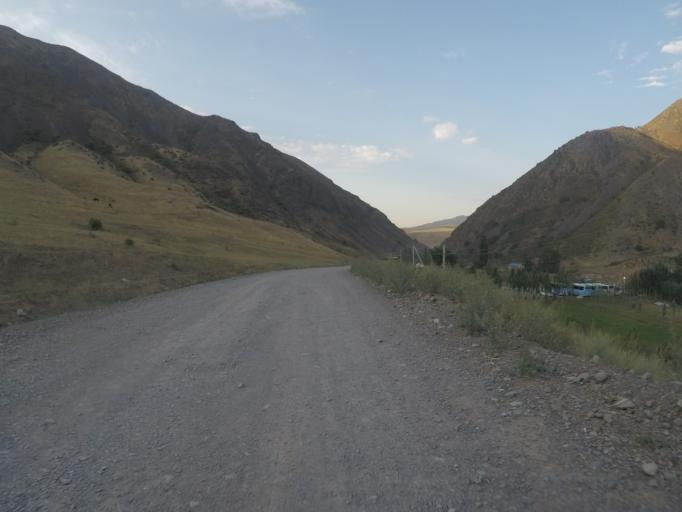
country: KG
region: Chuy
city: Bishkek
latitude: 42.6779
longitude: 74.6543
